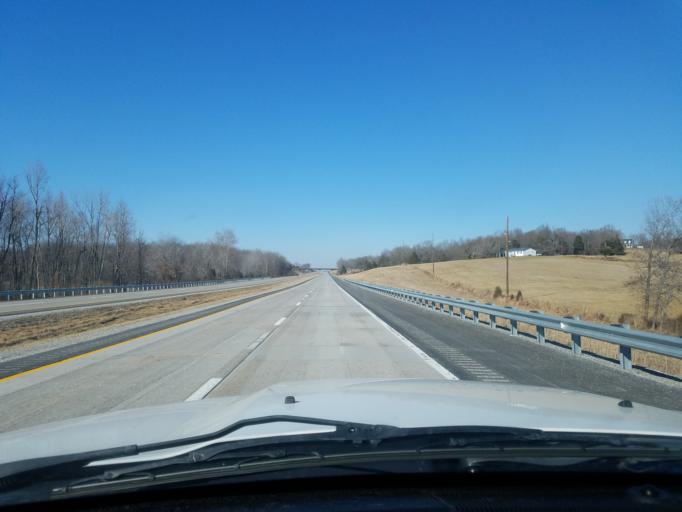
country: US
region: Kentucky
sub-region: Ohio County
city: Beaver Dam
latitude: 37.4033
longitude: -86.8227
